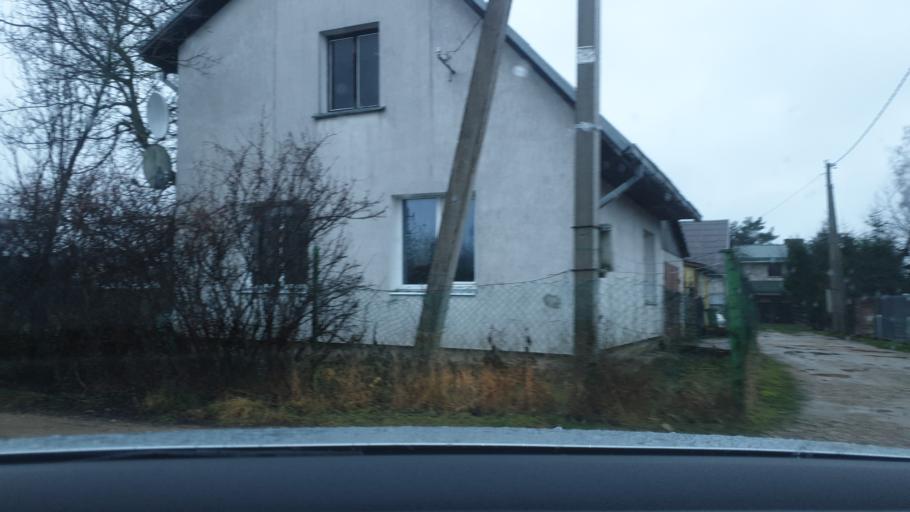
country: LT
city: Skaidiskes
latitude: 54.6654
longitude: 25.3667
